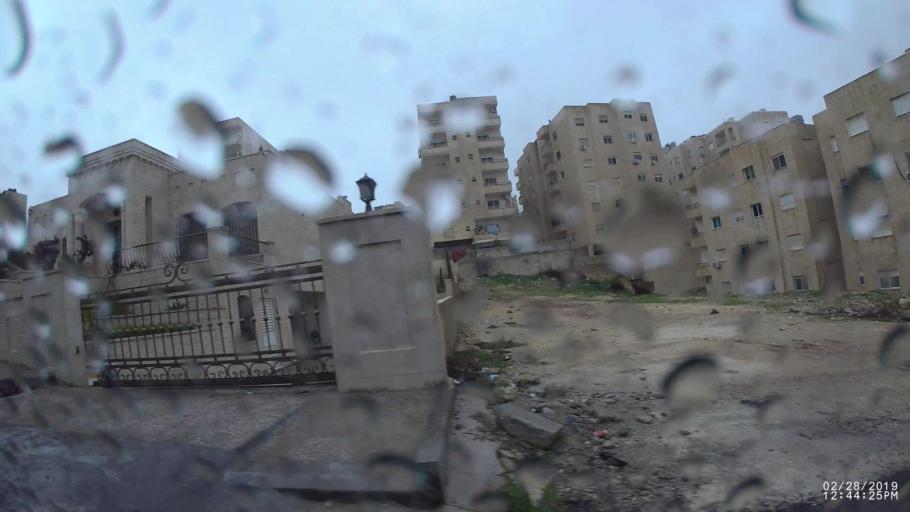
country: JO
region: Amman
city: Al Jubayhah
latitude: 32.0291
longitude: 35.8833
